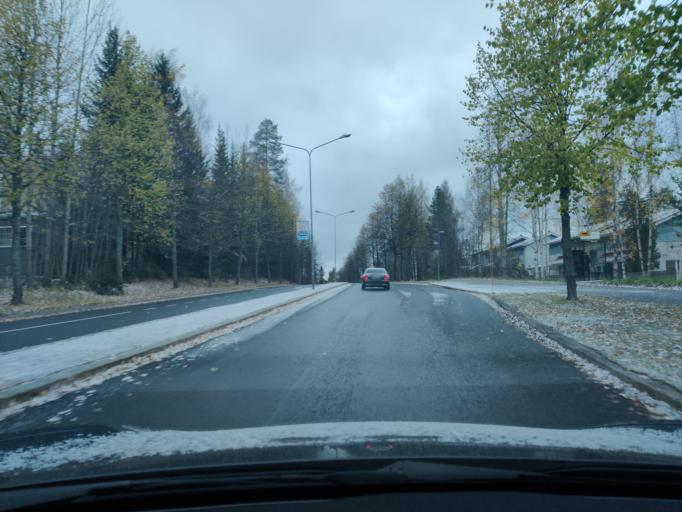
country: FI
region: Northern Savo
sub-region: Kuopio
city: Kuopio
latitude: 62.8393
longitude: 27.6354
